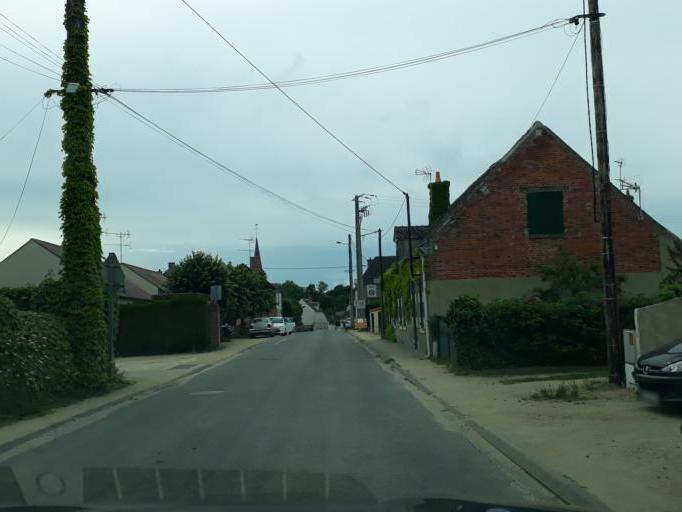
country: FR
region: Centre
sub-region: Departement du Loiret
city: Saint-Pere-sur-Loire
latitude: 47.7279
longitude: 2.3044
